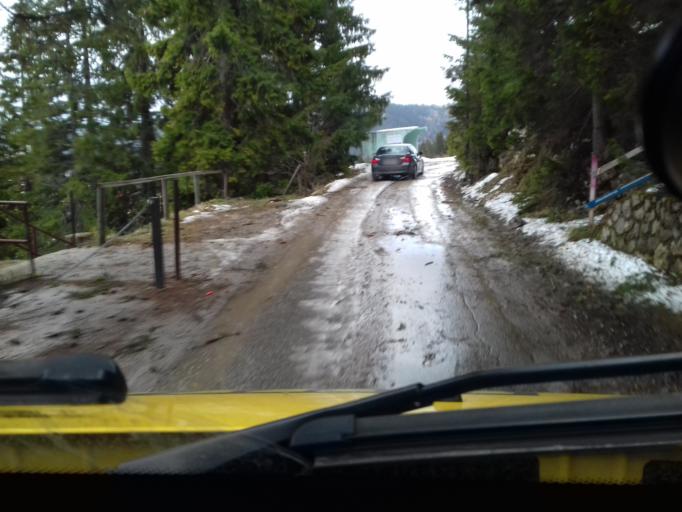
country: BA
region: Federation of Bosnia and Herzegovina
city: Turbe
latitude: 44.3096
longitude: 17.5757
